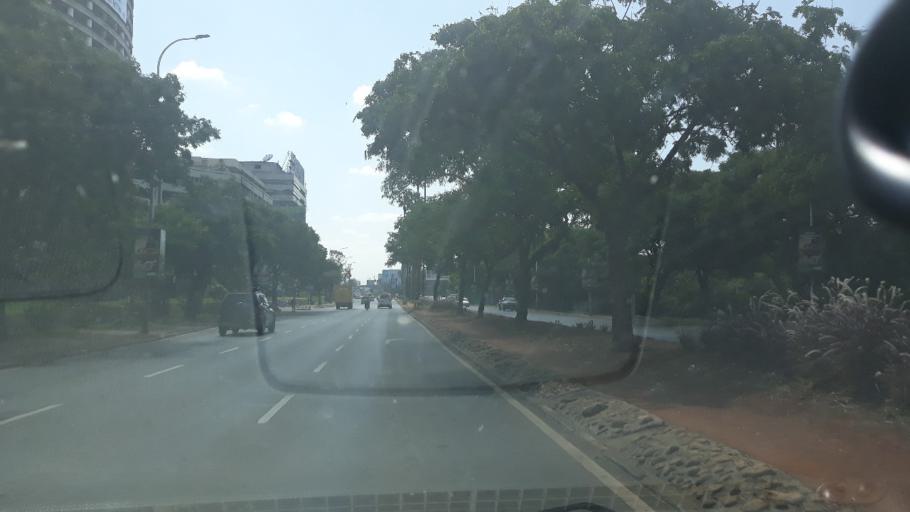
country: KE
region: Nairobi Area
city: Nairobi
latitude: -1.2904
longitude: 36.8192
